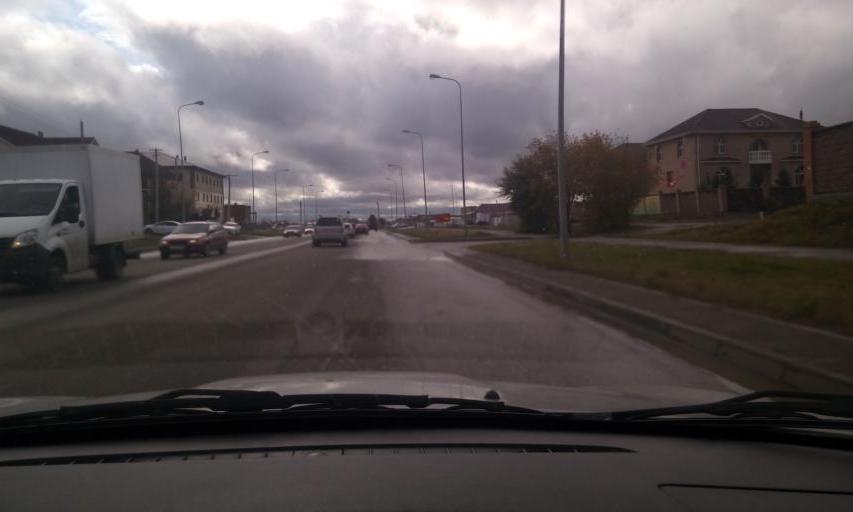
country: KZ
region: Astana Qalasy
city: Astana
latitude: 51.1771
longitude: 71.3685
